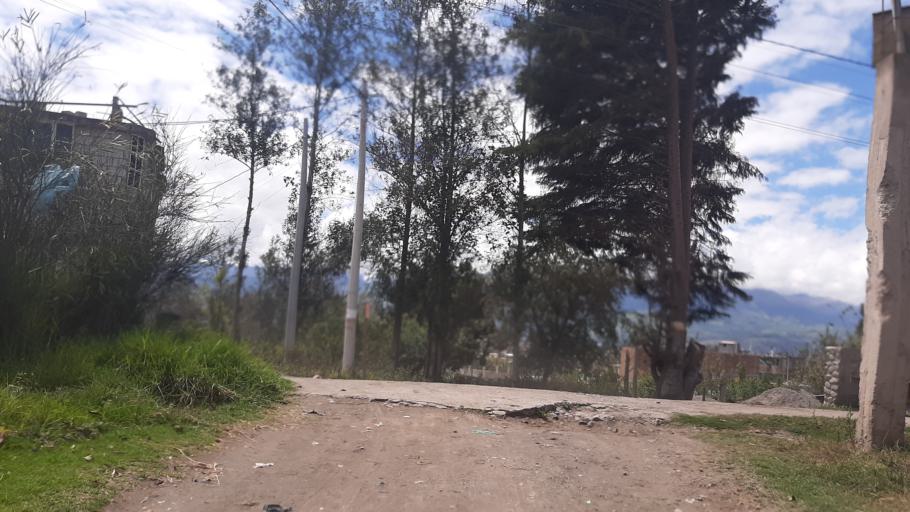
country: EC
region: Chimborazo
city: Riobamba
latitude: -1.6517
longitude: -78.6380
